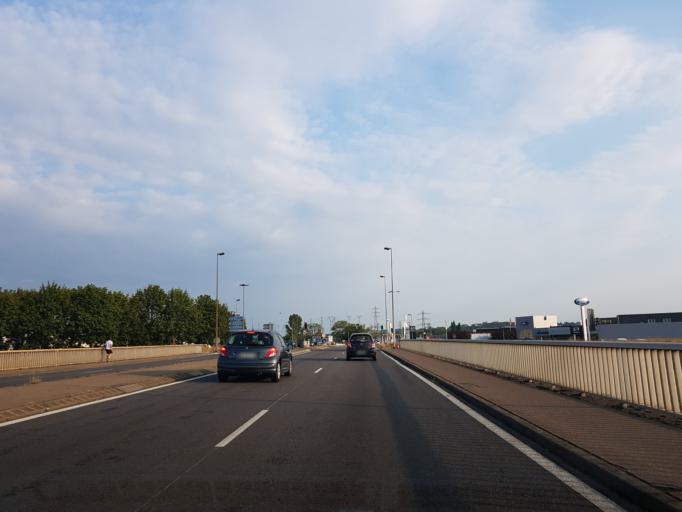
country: FR
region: Alsace
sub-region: Departement du Haut-Rhin
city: Sausheim
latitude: 47.7735
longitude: 7.3803
